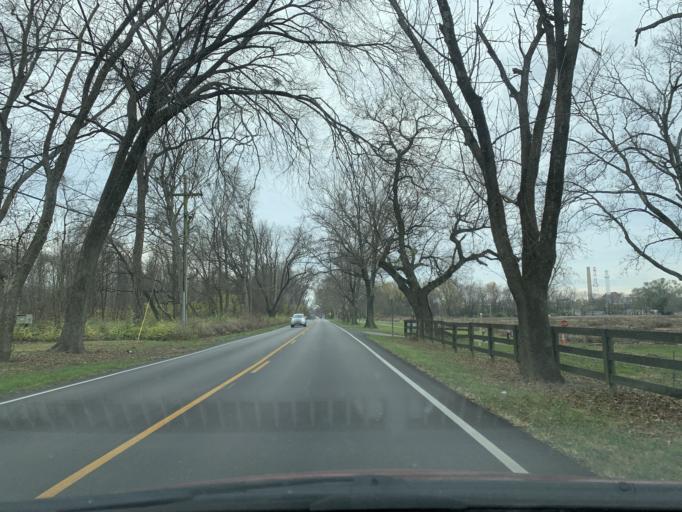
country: US
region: Indiana
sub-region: Clark County
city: Oak Park
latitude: 38.2822
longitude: -85.6927
